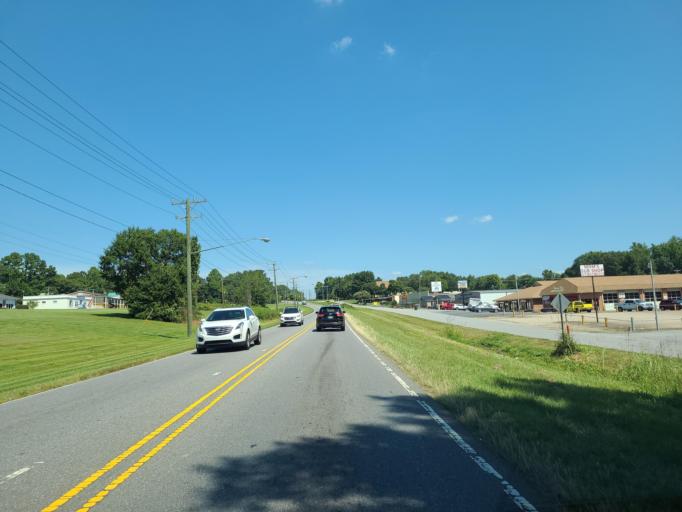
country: US
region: North Carolina
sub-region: Lincoln County
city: Lincolnton
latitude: 35.4684
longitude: -81.2398
